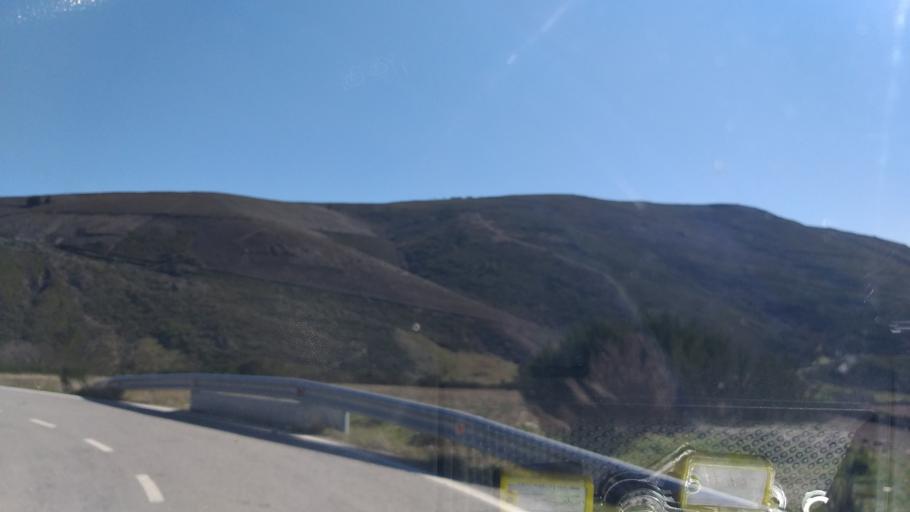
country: PT
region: Guarda
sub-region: Manteigas
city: Manteigas
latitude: 40.4582
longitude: -7.4948
